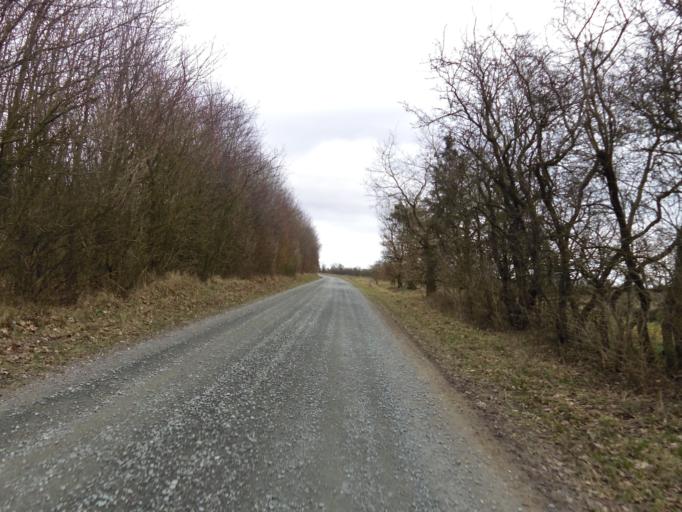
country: DK
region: South Denmark
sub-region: Tonder Kommune
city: Toftlund
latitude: 55.2129
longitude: 9.1666
